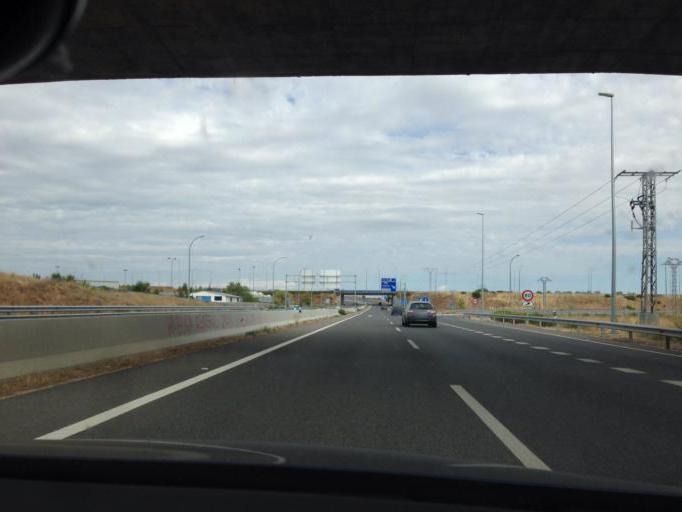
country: ES
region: Madrid
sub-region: Provincia de Madrid
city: Camarma de Esteruelas
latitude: 40.5193
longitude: -3.4104
